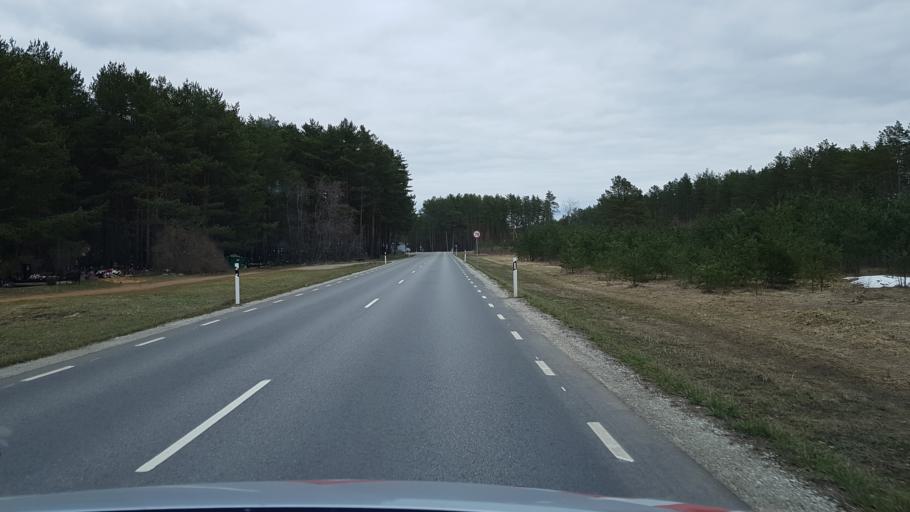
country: EE
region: Ida-Virumaa
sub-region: Narva-Joesuu linn
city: Narva-Joesuu
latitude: 59.4187
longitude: 28.1031
